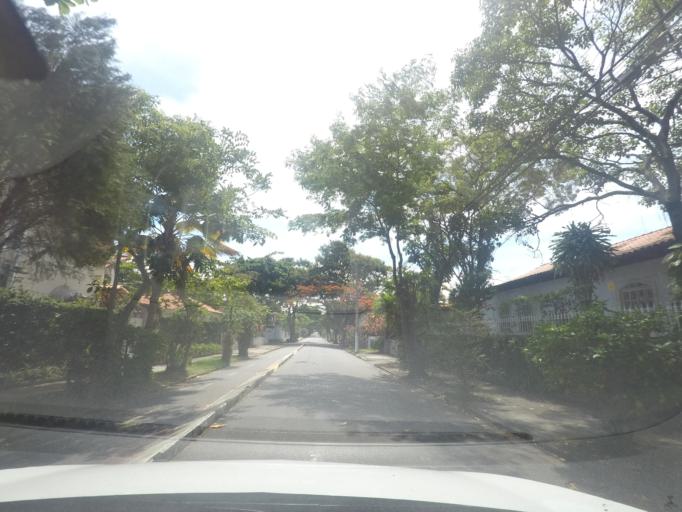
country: BR
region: Rio de Janeiro
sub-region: Niteroi
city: Niteroi
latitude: -22.9153
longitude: -43.0885
